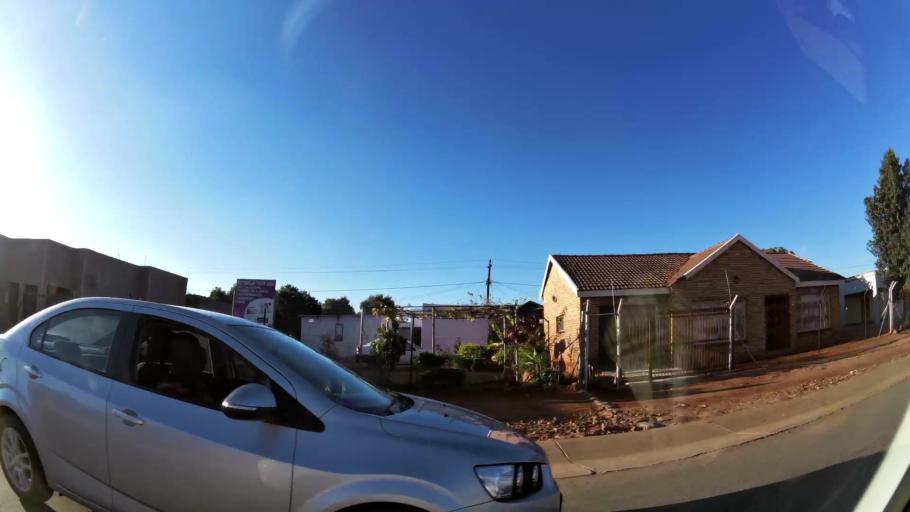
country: ZA
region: Limpopo
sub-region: Waterberg District Municipality
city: Mokopane
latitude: -24.1455
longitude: 28.9929
